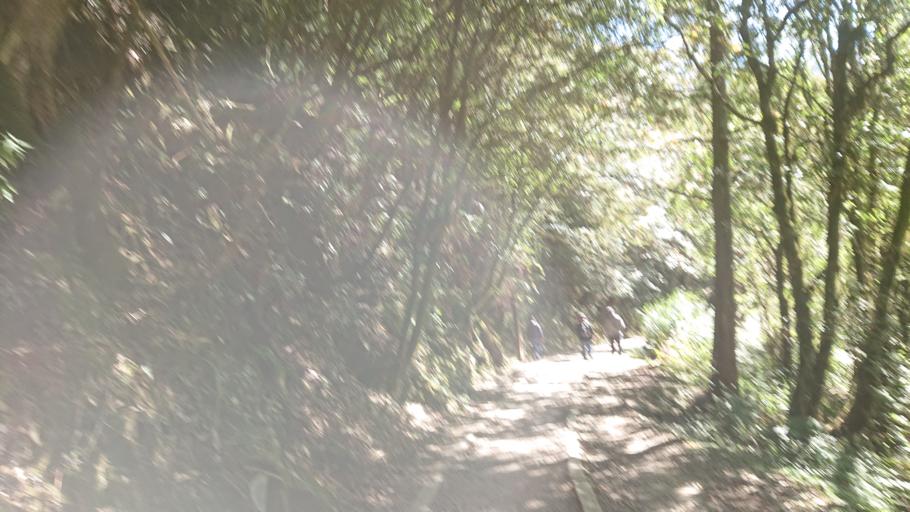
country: TW
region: Taiwan
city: Lugu
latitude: 23.4804
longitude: 120.8247
